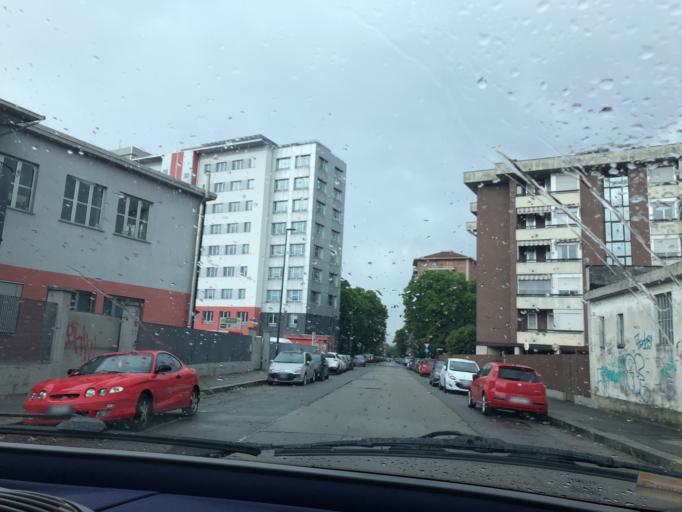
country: IT
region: Piedmont
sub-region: Provincia di Torino
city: Lesna
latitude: 45.0769
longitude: 7.6237
